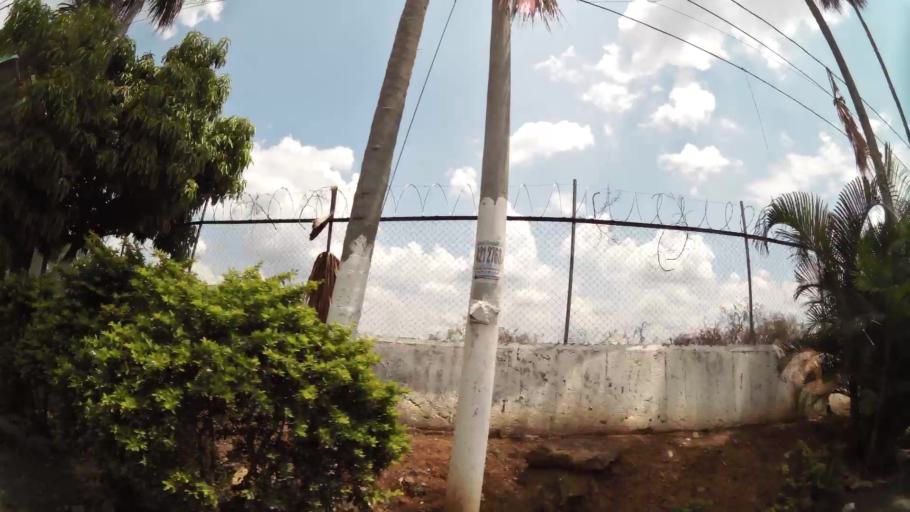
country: CO
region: Valle del Cauca
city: Cali
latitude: 3.4542
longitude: -76.4739
